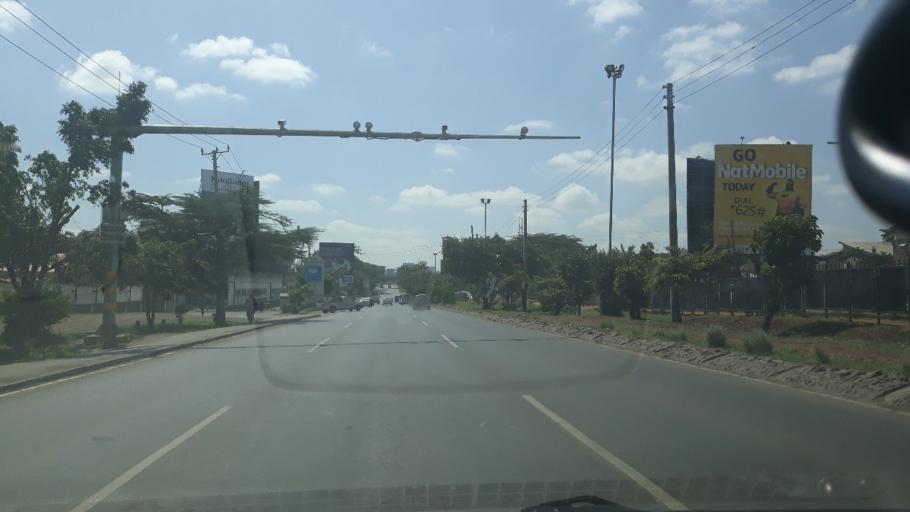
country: KE
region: Nairobi Area
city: Nairobi
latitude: -1.3078
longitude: 36.8279
